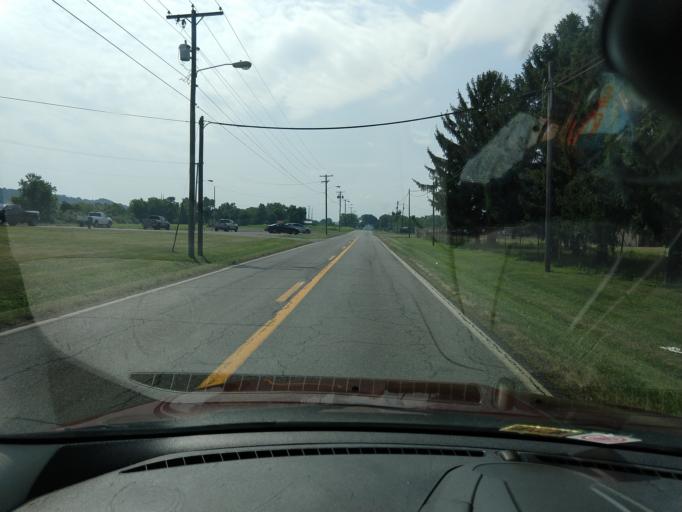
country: US
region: West Virginia
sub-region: Mason County
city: New Haven
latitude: 38.9588
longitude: -81.9244
